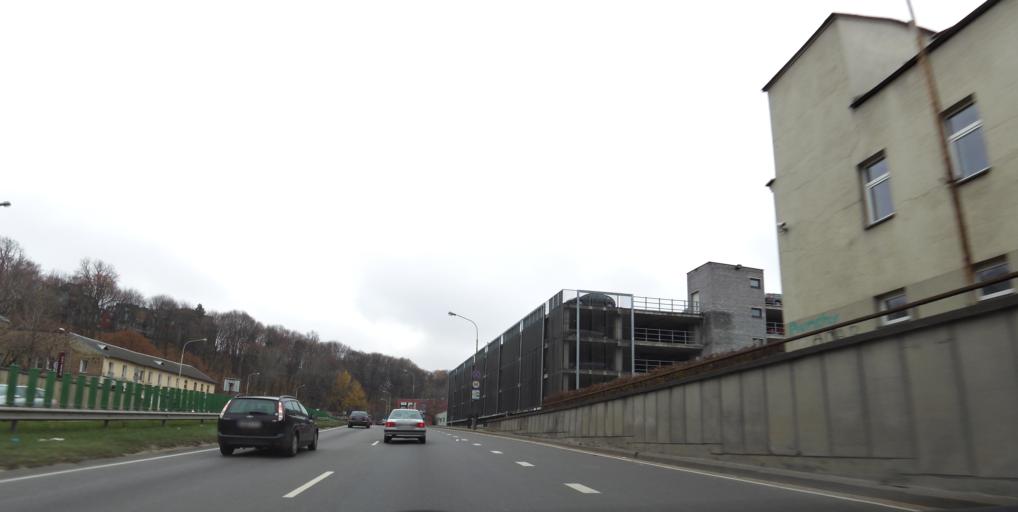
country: LT
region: Vilnius County
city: Naujamiestis
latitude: 54.6873
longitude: 25.2620
